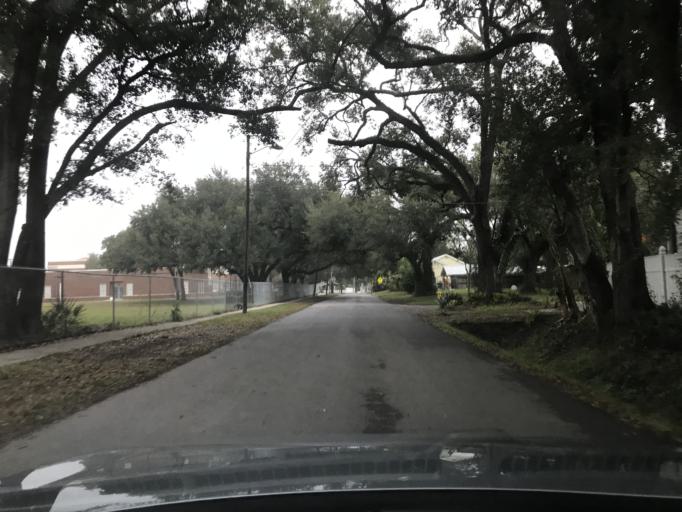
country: US
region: Florida
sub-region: Hillsborough County
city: Tampa
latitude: 27.9870
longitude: -82.4635
